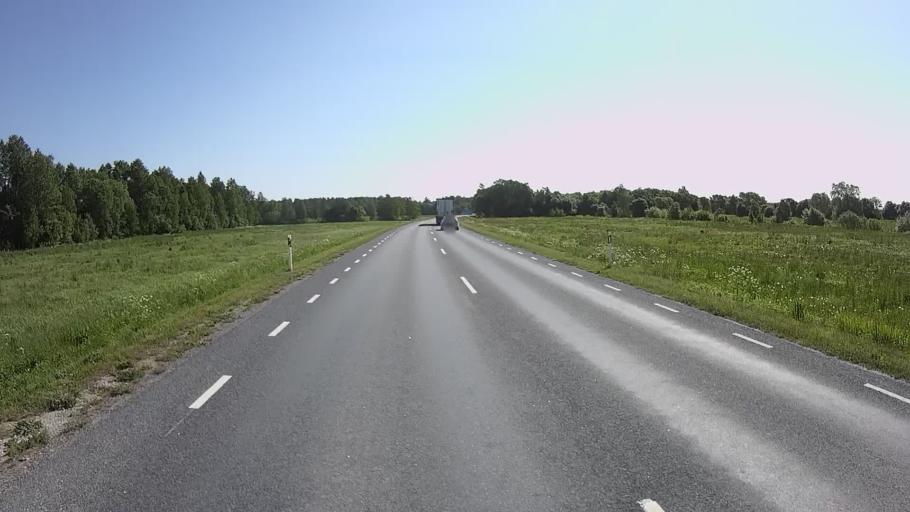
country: EE
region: Saare
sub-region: Orissaare vald
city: Orissaare
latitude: 58.6083
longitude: 23.2717
